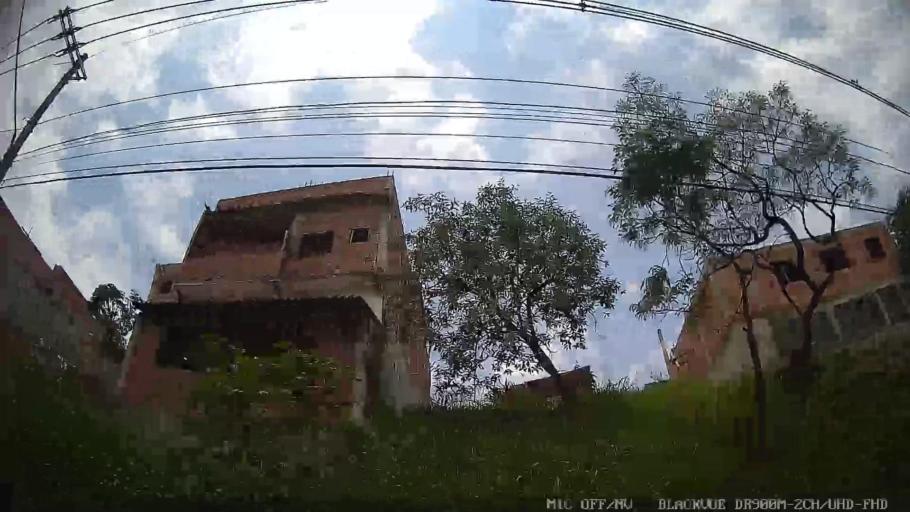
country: BR
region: Sao Paulo
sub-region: Caieiras
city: Caieiras
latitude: -23.4235
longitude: -46.7272
